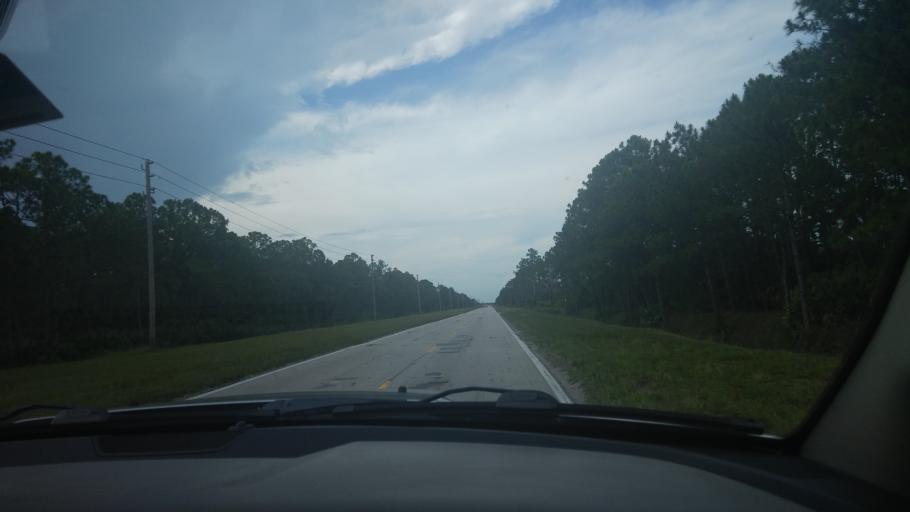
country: US
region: Florida
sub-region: Brevard County
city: Grant-Valkaria
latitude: 27.8778
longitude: -80.6227
